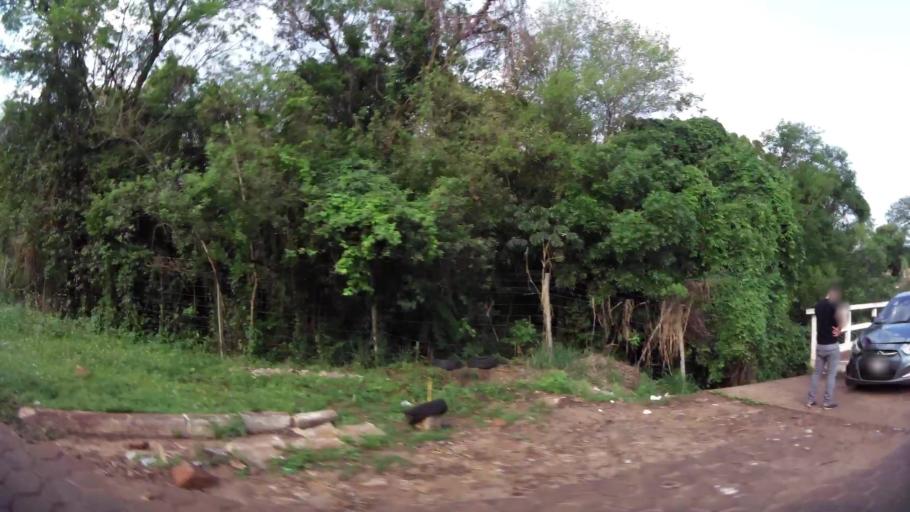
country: PY
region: Alto Parana
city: Presidente Franco
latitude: -25.5242
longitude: -54.6352
